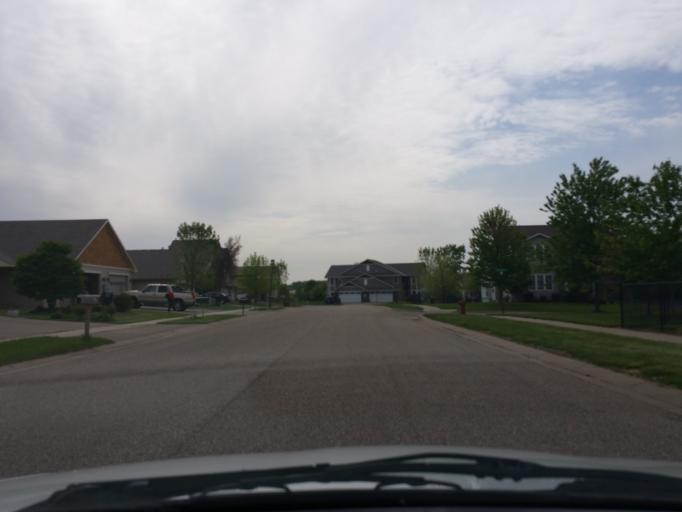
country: US
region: Wisconsin
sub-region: Saint Croix County
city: Hudson
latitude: 44.9511
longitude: -92.6918
